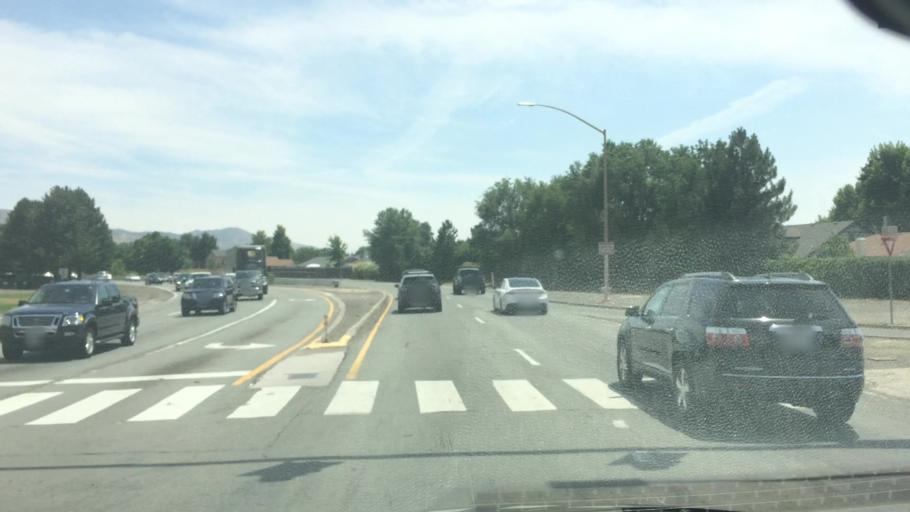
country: US
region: Nevada
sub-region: Washoe County
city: Sparks
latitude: 39.5564
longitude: -119.7245
